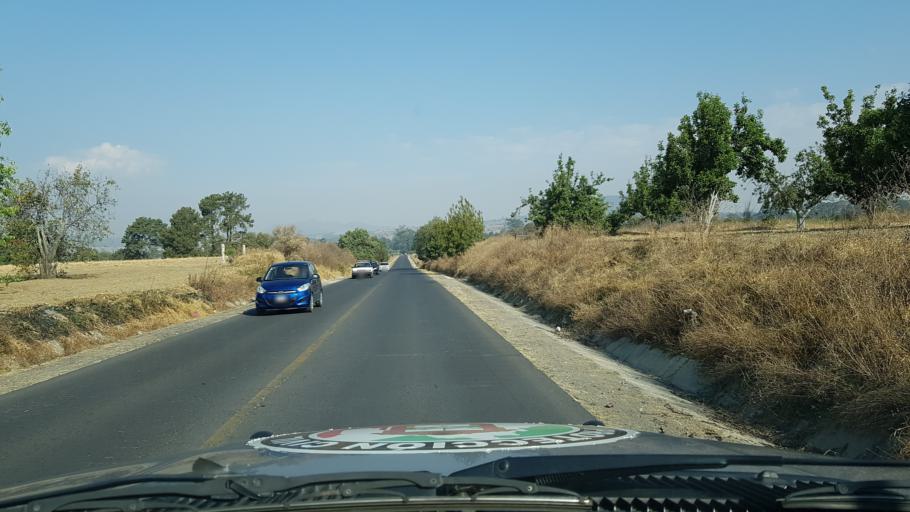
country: MX
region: Mexico
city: Ozumba de Alzate
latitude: 19.0463
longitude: -98.7759
